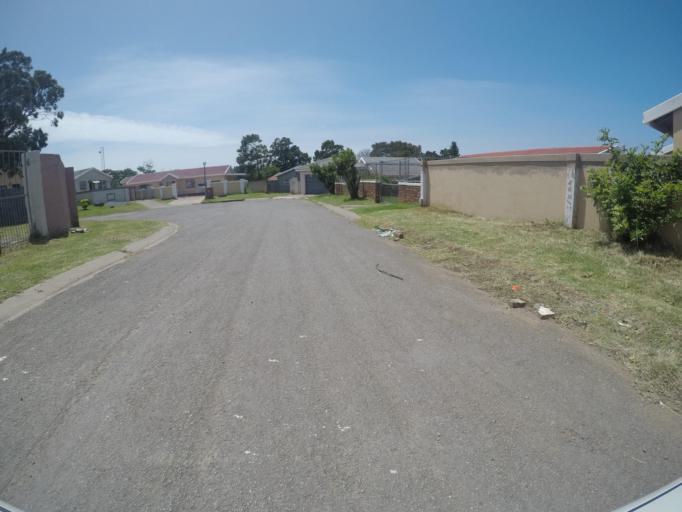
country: ZA
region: Eastern Cape
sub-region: Buffalo City Metropolitan Municipality
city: East London
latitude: -32.9364
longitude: 27.9918
